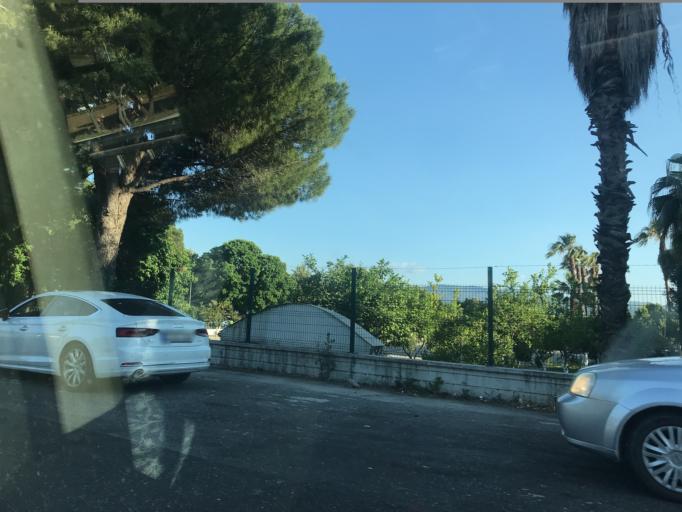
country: TR
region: Mugla
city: Ula
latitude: 37.0504
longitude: 28.3567
